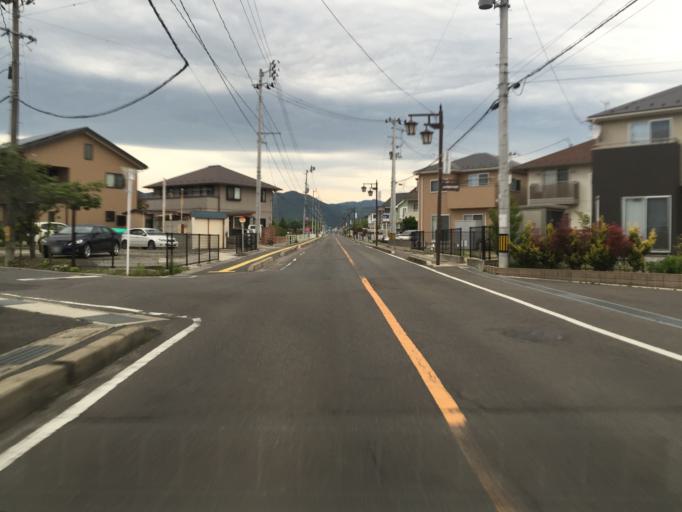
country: JP
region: Fukushima
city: Fukushima-shi
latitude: 37.7913
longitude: 140.4343
